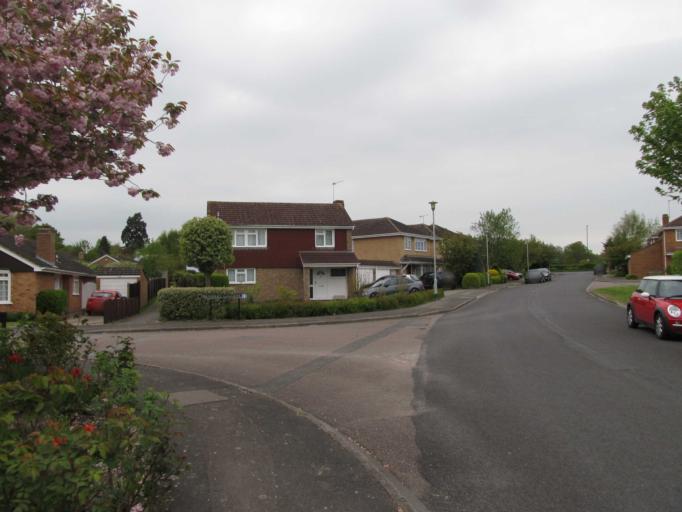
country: GB
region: England
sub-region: Royal Borough of Windsor and Maidenhead
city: Maidenhead
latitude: 51.5328
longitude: -0.7512
